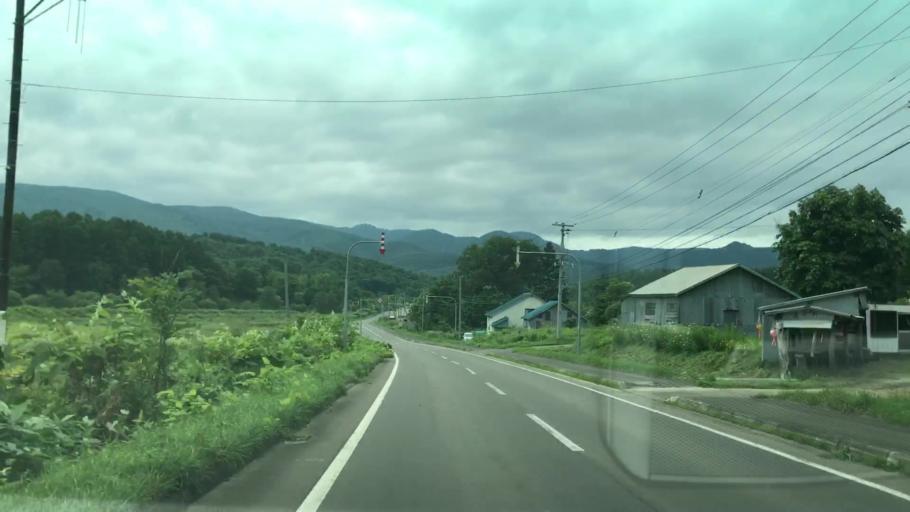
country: JP
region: Hokkaido
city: Yoichi
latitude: 43.0636
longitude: 140.8210
